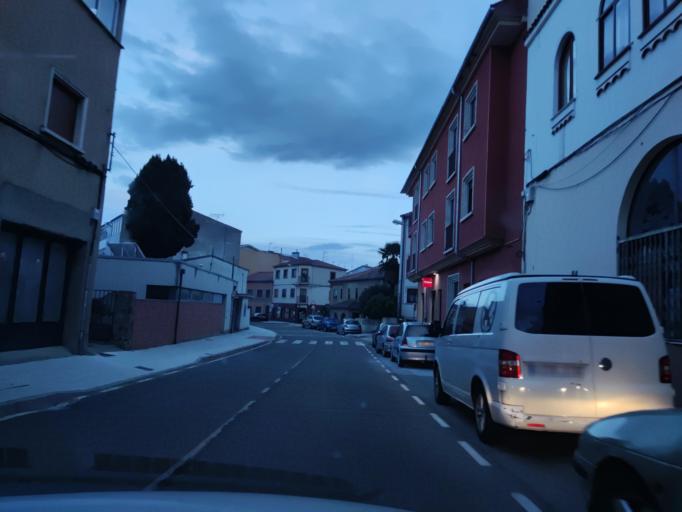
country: ES
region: Castille and Leon
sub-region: Provincia de Salamanca
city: Ciudad Rodrigo
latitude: 40.5980
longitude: -6.5296
